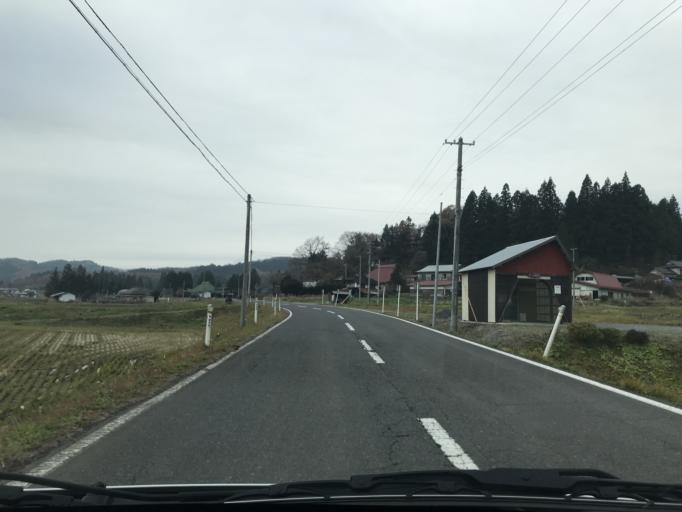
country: JP
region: Iwate
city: Kitakami
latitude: 39.2596
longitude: 141.2002
